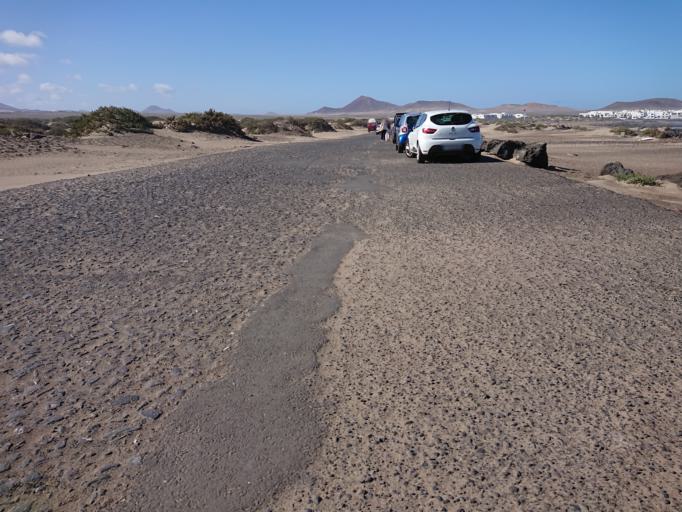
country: ES
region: Canary Islands
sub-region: Provincia de Las Palmas
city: Teguise
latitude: 29.1150
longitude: -13.5559
